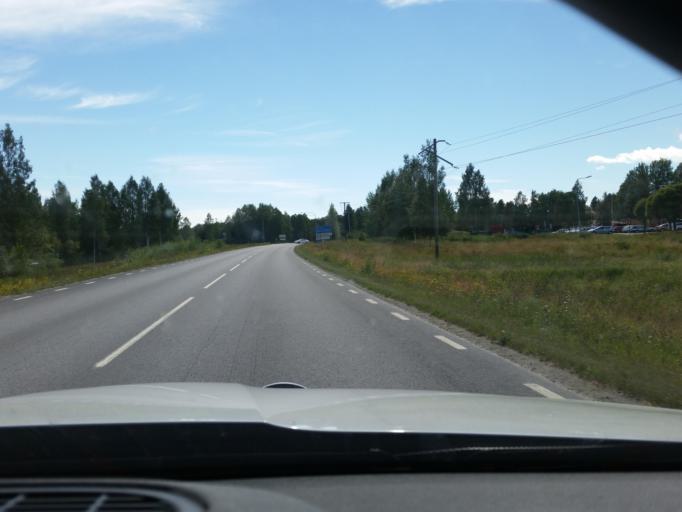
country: SE
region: Norrbotten
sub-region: Pitea Kommun
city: Norrfjarden
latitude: 65.4245
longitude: 21.4958
